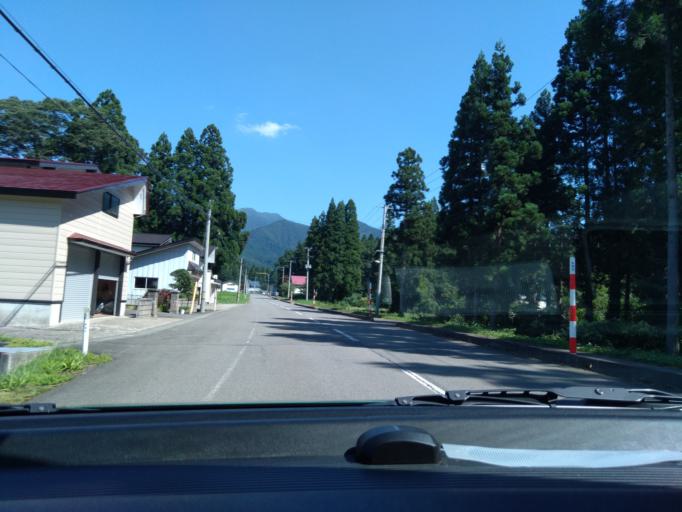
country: JP
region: Akita
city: Omagari
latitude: 39.4636
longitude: 140.6176
